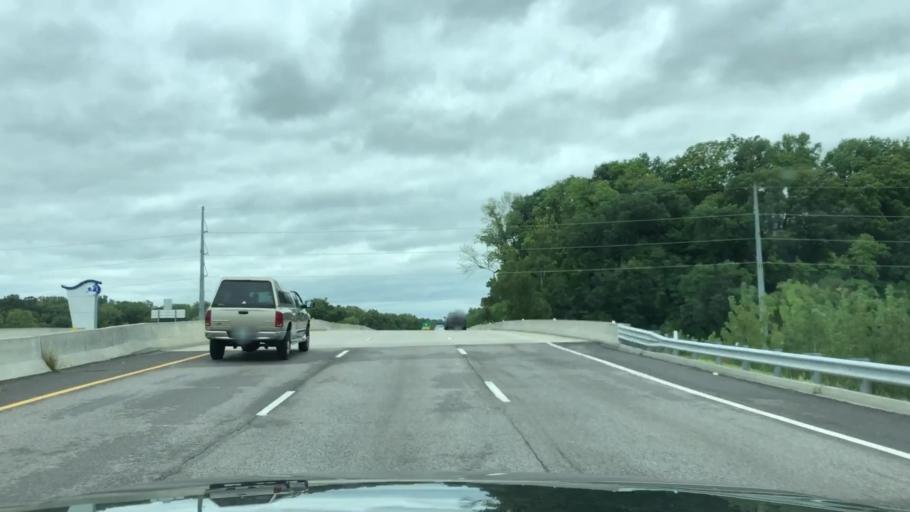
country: US
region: Missouri
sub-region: Saint Louis County
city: Maryland Heights
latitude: 38.6934
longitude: -90.5001
